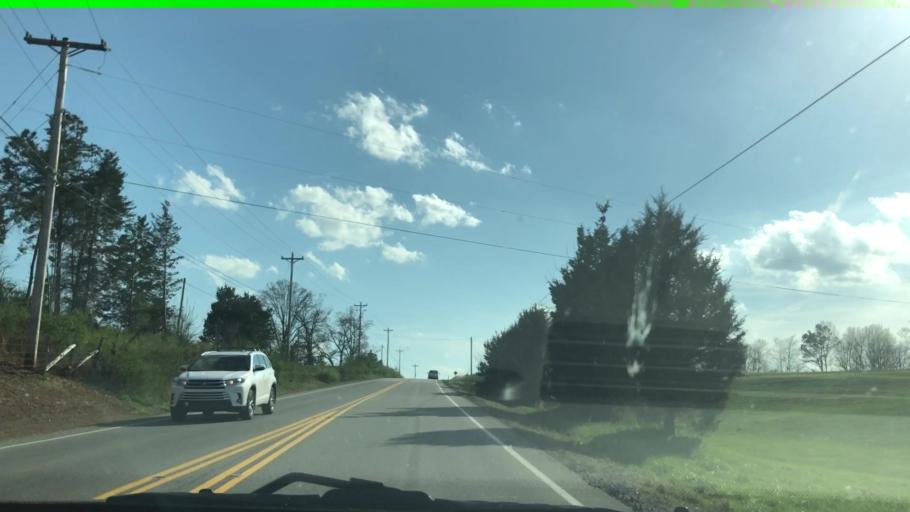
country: US
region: Tennessee
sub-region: Putnam County
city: Baxter
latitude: 36.0926
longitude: -85.5812
